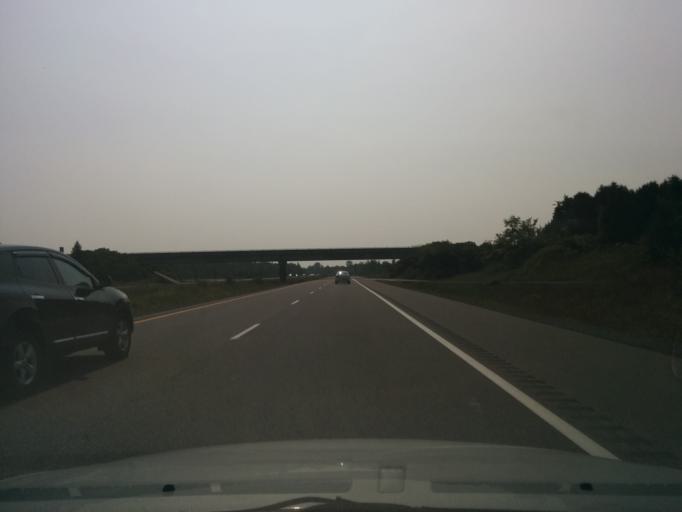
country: CA
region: Ontario
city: Bells Corners
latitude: 45.0945
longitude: -75.6540
